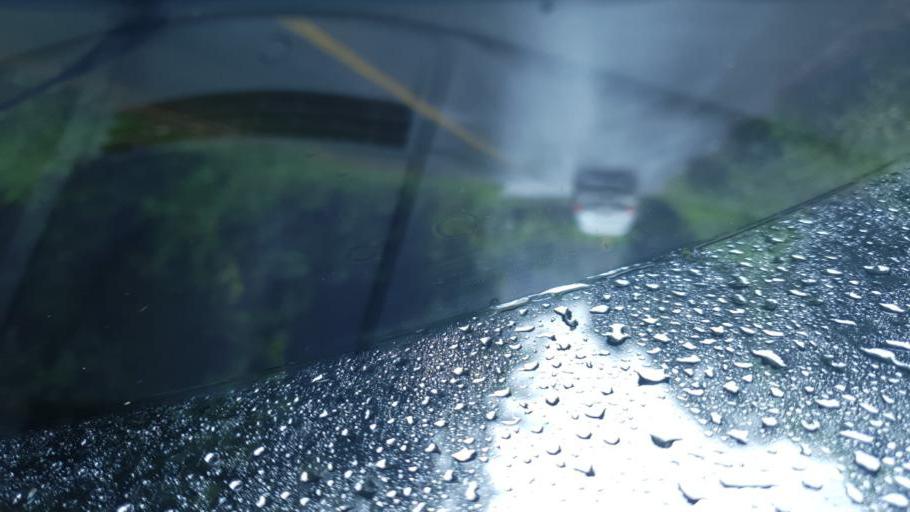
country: TH
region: Mae Hong Son
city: Khun Yuam
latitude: 18.6435
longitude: 97.9426
